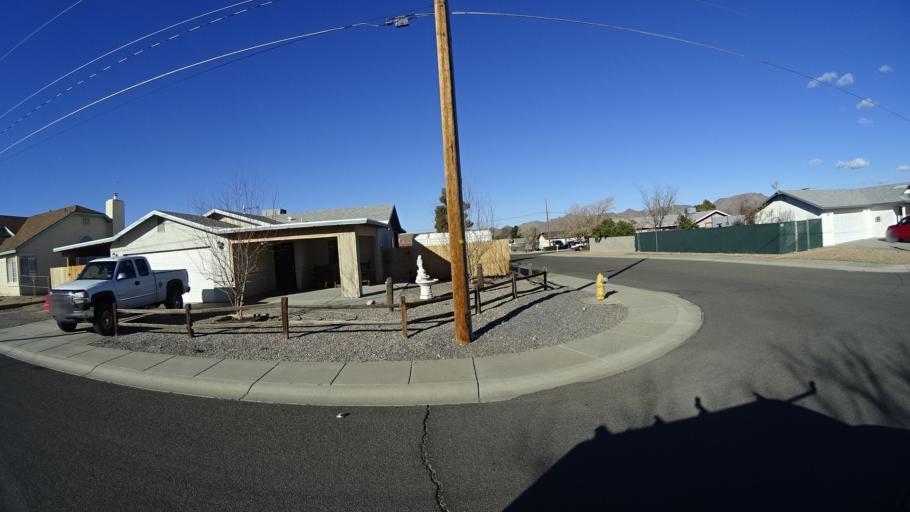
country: US
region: Arizona
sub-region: Mohave County
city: New Kingman-Butler
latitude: 35.2192
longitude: -113.9951
